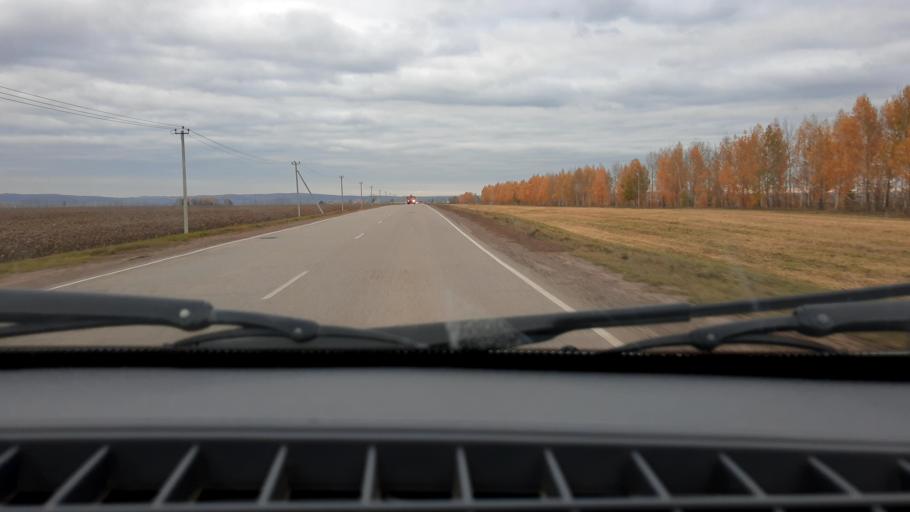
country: RU
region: Bashkortostan
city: Kabakovo
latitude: 54.5385
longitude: 56.0736
